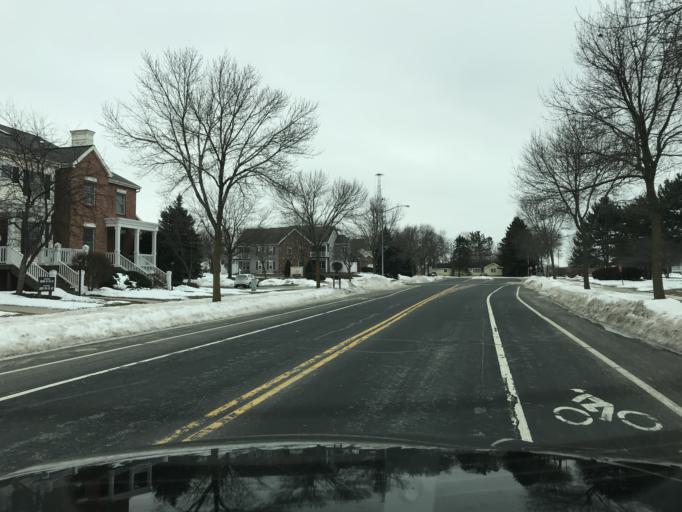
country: US
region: Wisconsin
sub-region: Dane County
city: Monona
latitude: 43.0764
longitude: -89.2764
